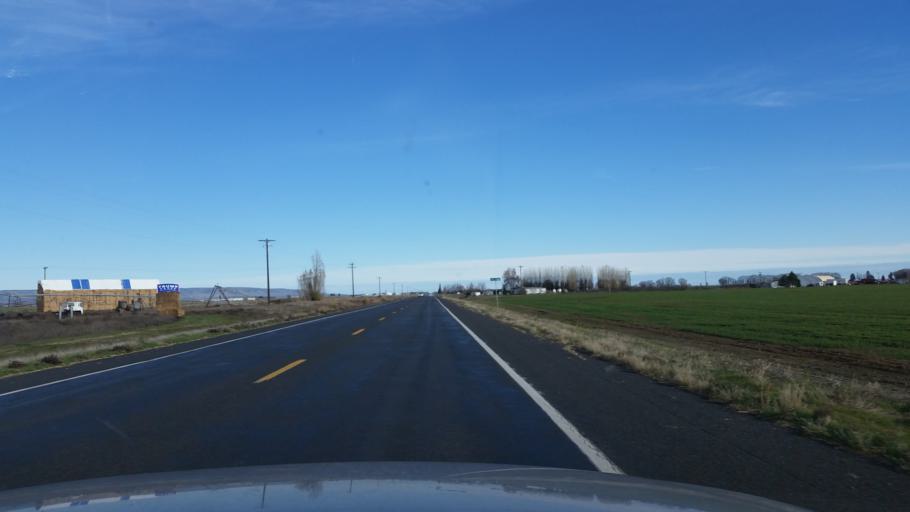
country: US
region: Washington
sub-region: Grant County
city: Quincy
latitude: 47.1306
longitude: -119.7883
